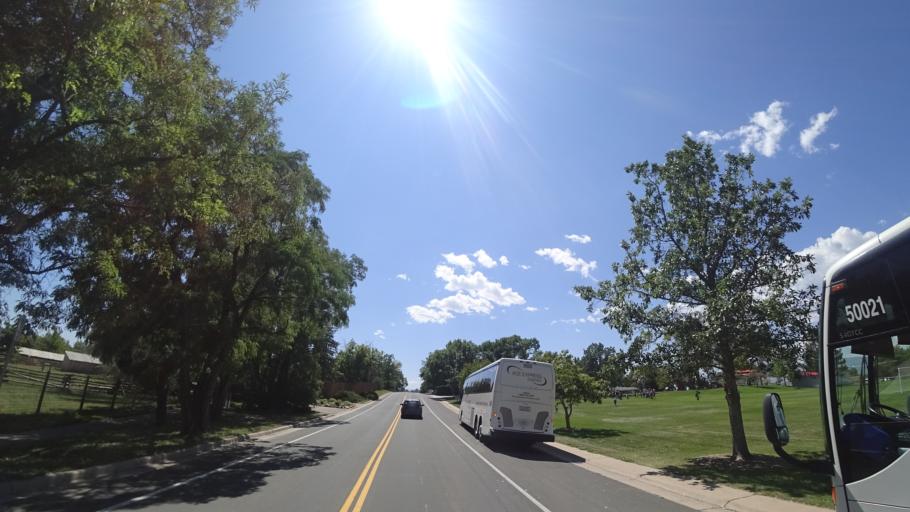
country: US
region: Colorado
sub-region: Arapahoe County
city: Littleton
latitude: 39.6060
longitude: -105.0021
